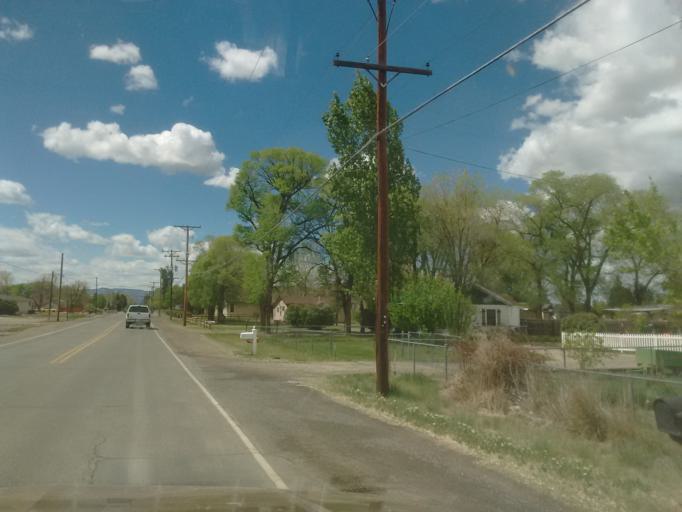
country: US
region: Colorado
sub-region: Mesa County
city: Fruitvale
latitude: 39.0774
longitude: -108.4756
